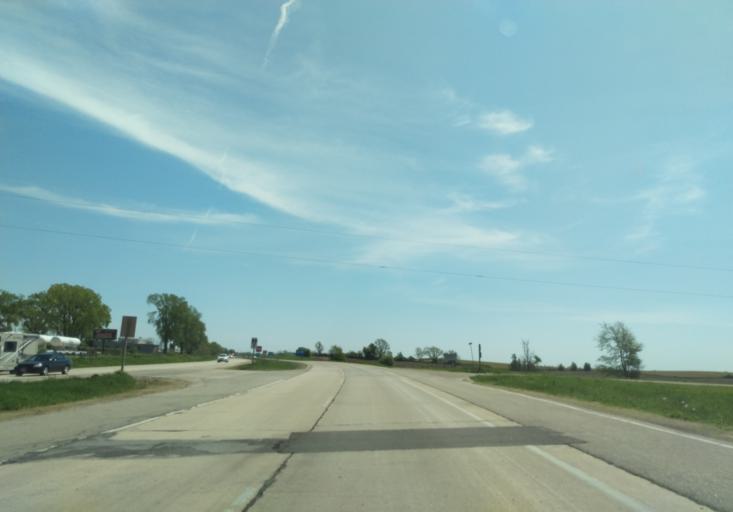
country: US
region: Wisconsin
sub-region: Dane County
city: Mount Horeb
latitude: 43.0069
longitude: -89.7855
